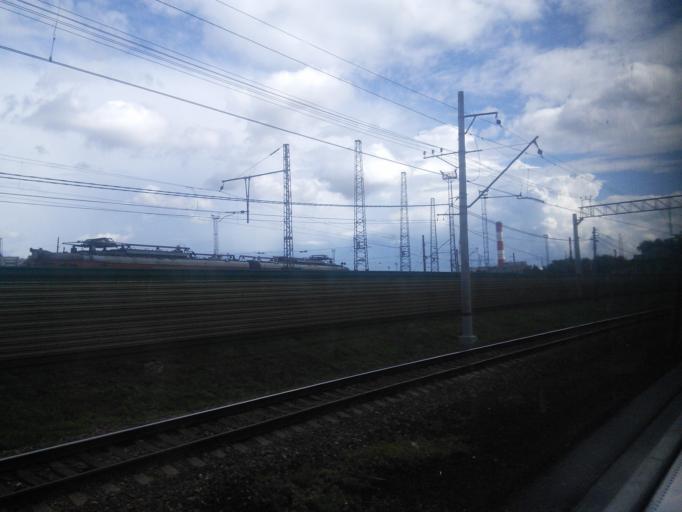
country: RU
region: Moscow
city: Lefortovo
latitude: 55.7653
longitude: 37.7212
